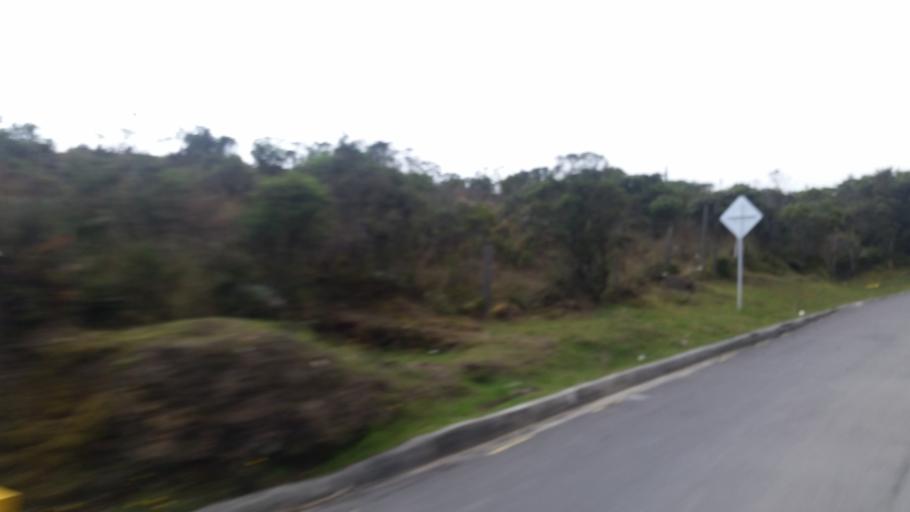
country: CO
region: Cundinamarca
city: Choachi
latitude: 4.5634
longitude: -73.9924
